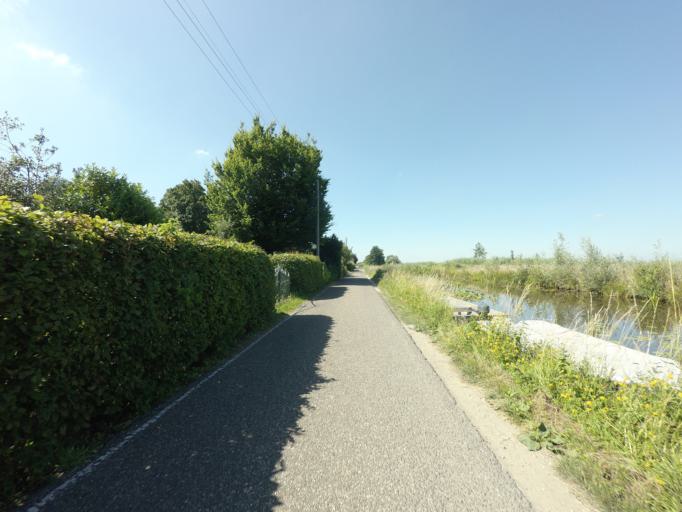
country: NL
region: South Holland
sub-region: Bodegraven-Reeuwijk
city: Reeuwijk
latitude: 52.0219
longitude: 4.7452
